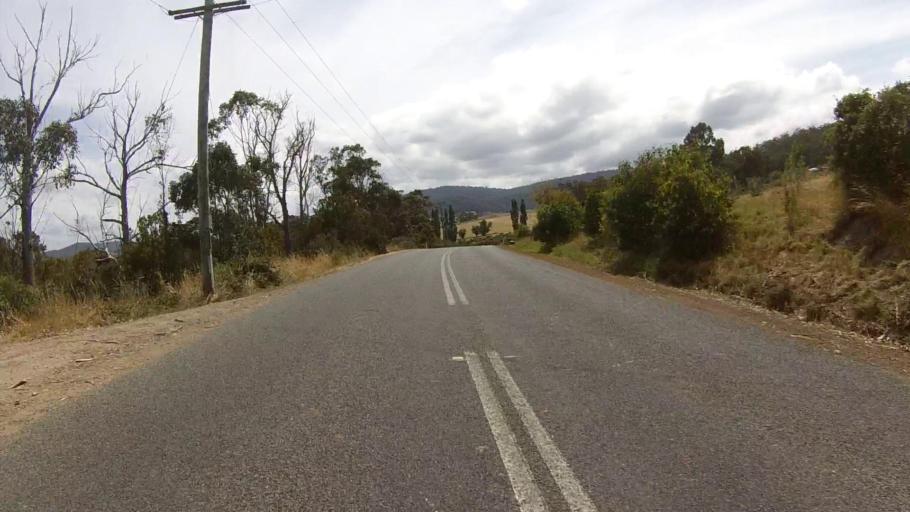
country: AU
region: Tasmania
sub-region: Huon Valley
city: Cygnet
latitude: -43.1799
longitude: 147.0928
